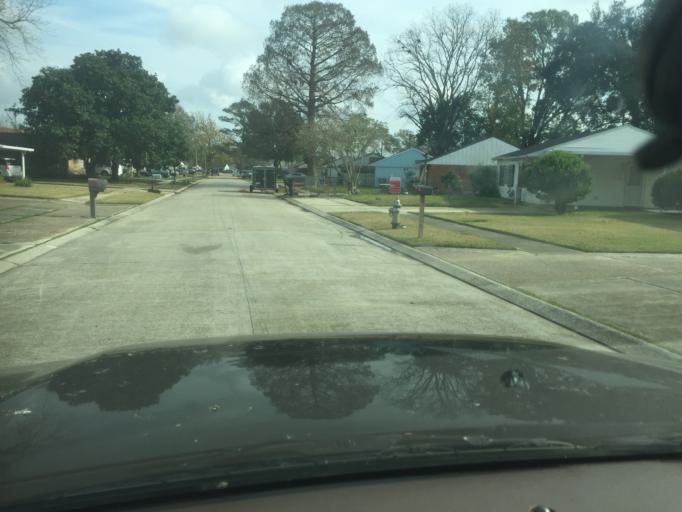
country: US
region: Louisiana
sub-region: Jefferson Parish
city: Avondale
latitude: 29.9146
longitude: -90.2041
